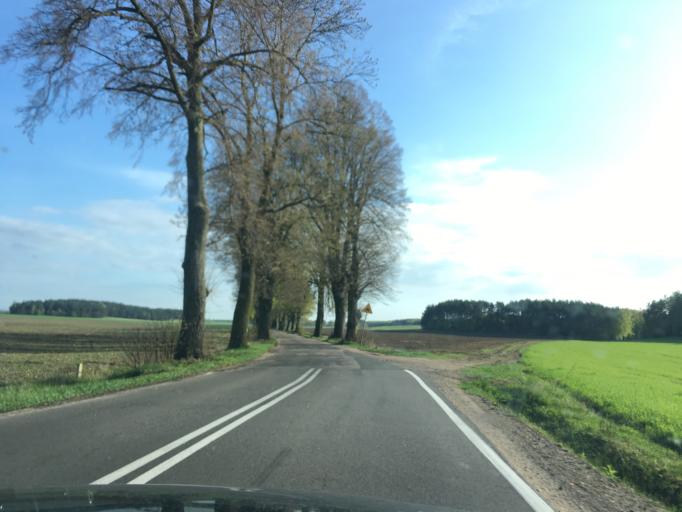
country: PL
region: Warmian-Masurian Voivodeship
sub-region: Powiat nidzicki
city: Nidzica
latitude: 53.4158
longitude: 20.3399
